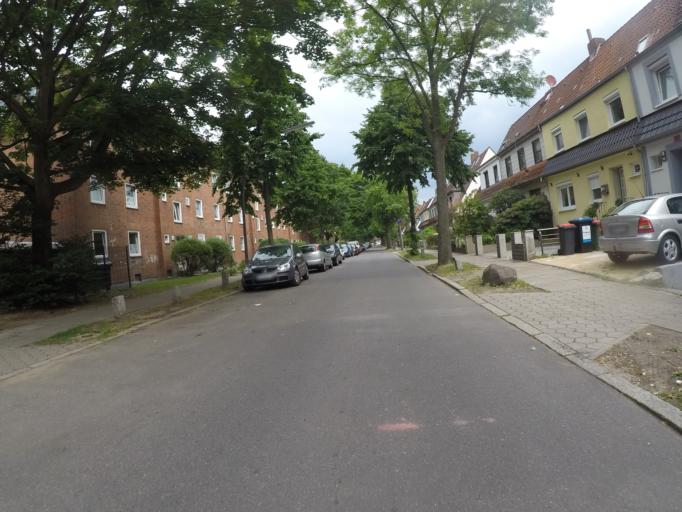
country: DE
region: Hamburg
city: Kleiner Grasbrook
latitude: 53.5106
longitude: 9.9881
